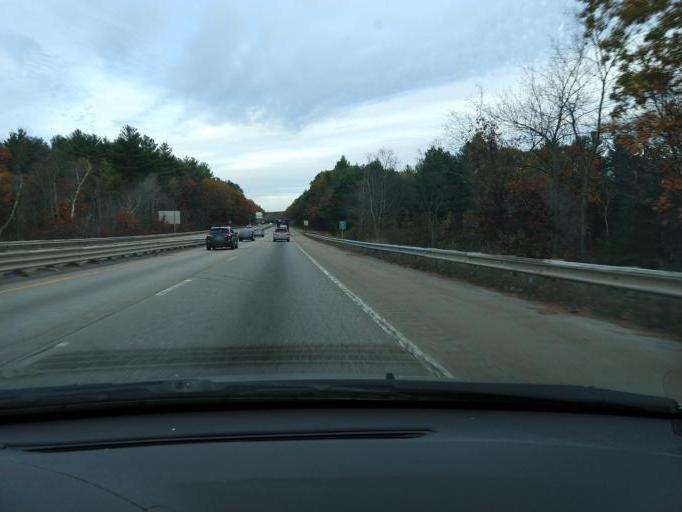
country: US
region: Massachusetts
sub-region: Worcester County
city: Harvard
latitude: 42.5232
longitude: -71.5736
